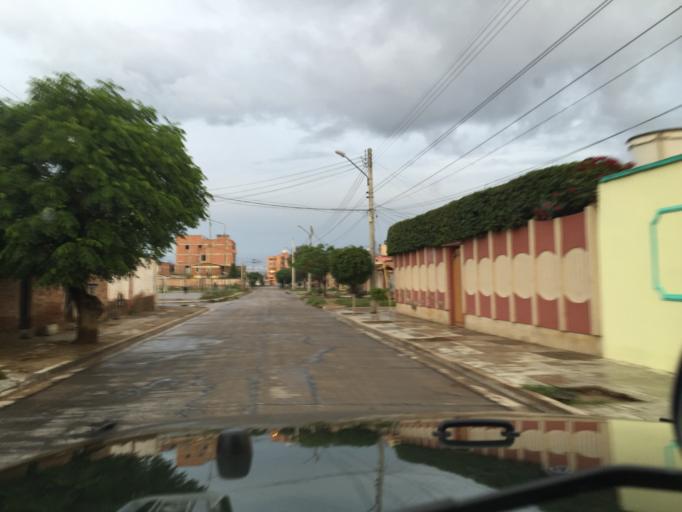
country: BO
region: Cochabamba
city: Cochabamba
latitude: -17.4192
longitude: -66.1643
